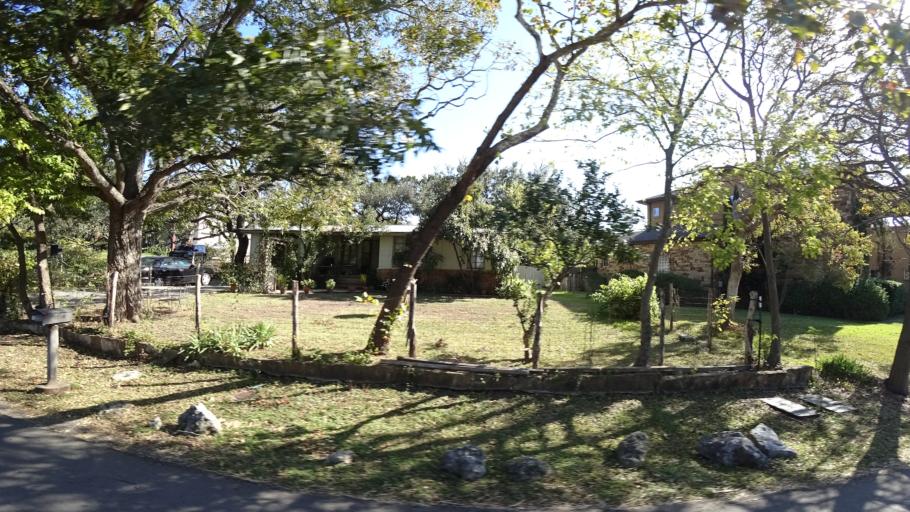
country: US
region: Texas
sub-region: Travis County
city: Hudson Bend
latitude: 30.3940
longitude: -97.8857
